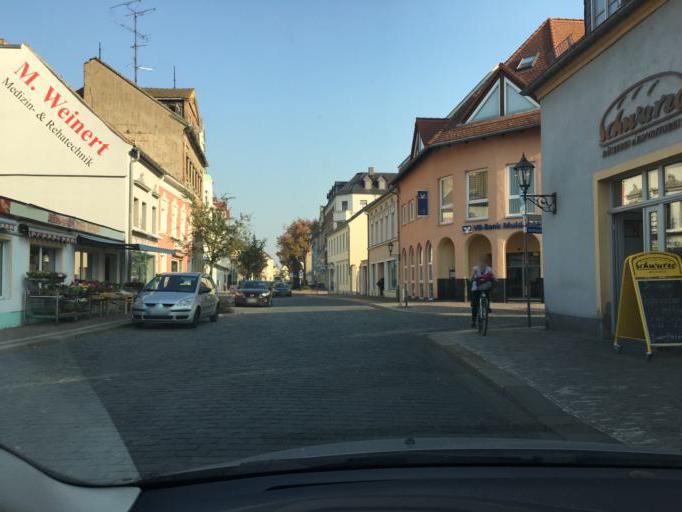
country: DE
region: Saxony
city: Wurzen
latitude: 51.3705
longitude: 12.7392
